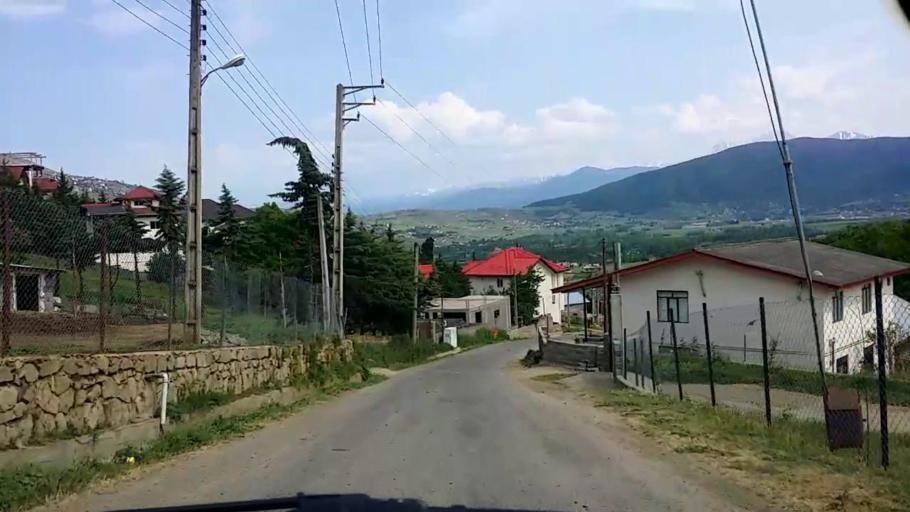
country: IR
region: Mazandaran
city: `Abbasabad
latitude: 36.5518
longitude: 51.1827
